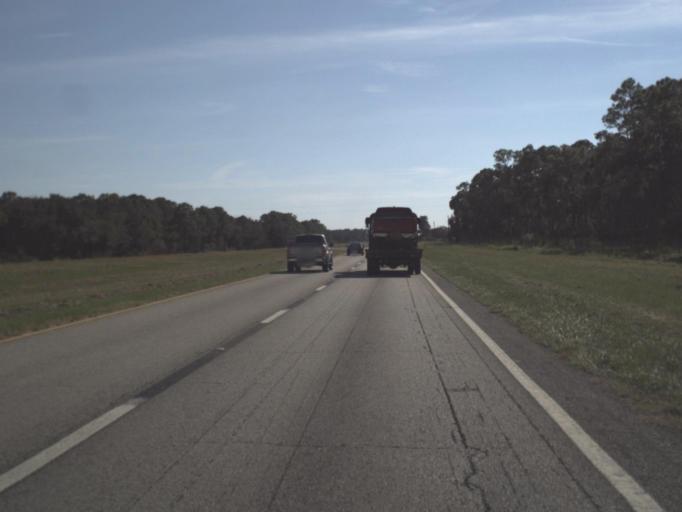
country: US
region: Florida
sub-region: Highlands County
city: Placid Lakes
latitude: 27.0584
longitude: -81.3386
